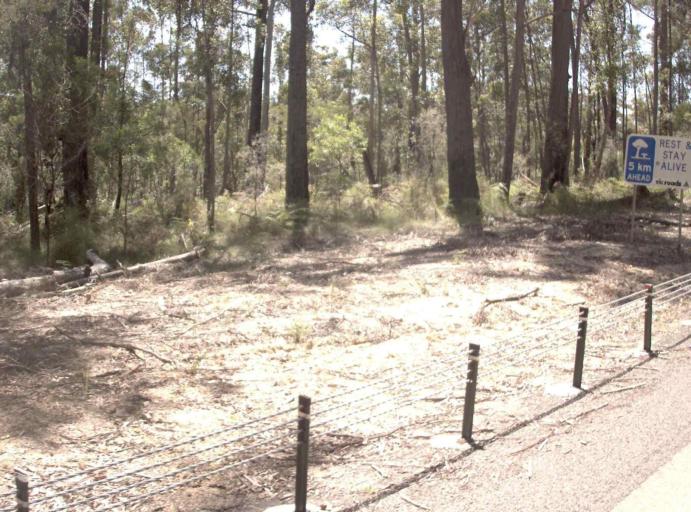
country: AU
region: Victoria
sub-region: East Gippsland
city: Lakes Entrance
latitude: -37.7045
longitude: 148.5771
